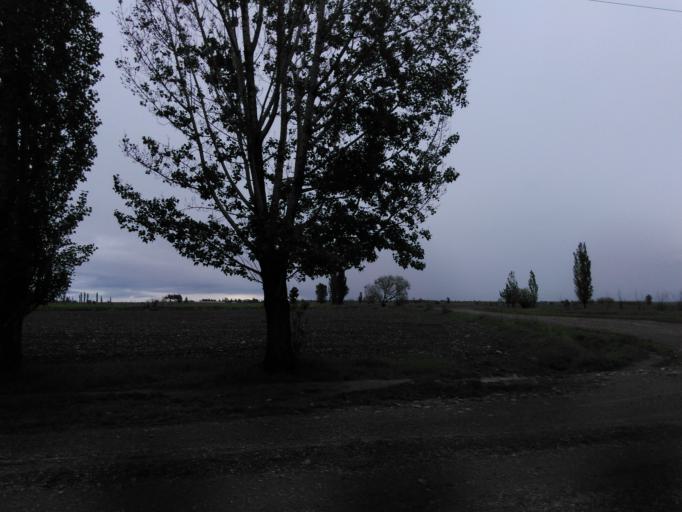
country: KG
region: Chuy
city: Chuy
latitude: 42.7476
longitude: 75.2727
